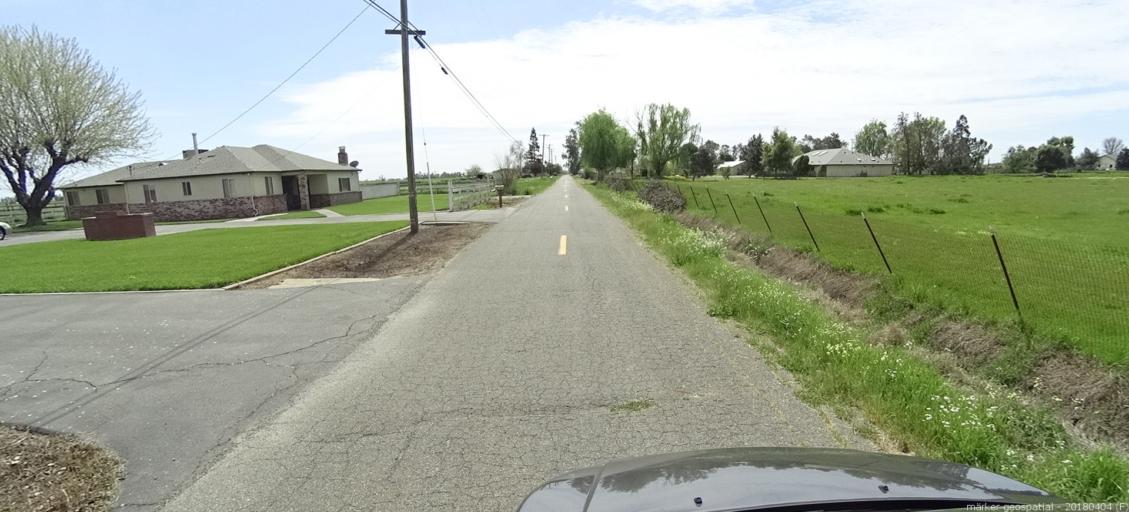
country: US
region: California
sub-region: Sacramento County
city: Herald
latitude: 38.2713
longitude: -121.2542
